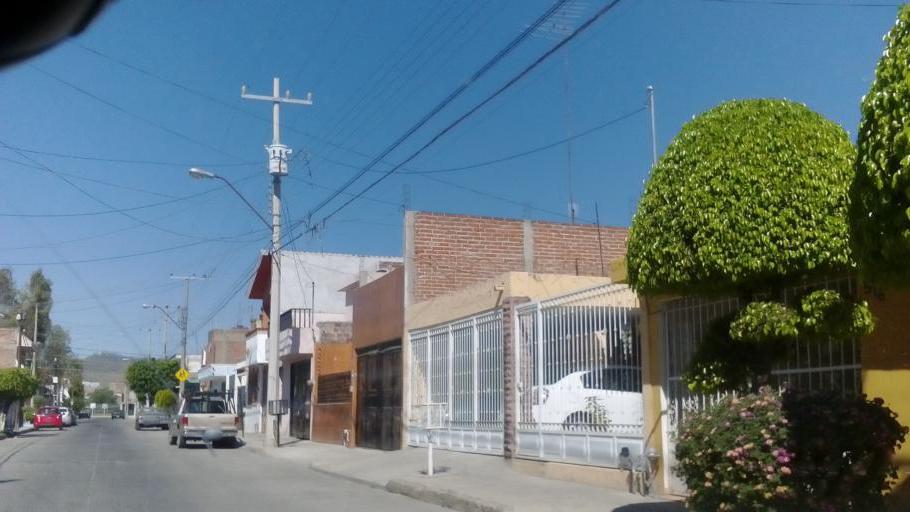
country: MX
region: Guanajuato
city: Leon
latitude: 21.1447
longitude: -101.6770
